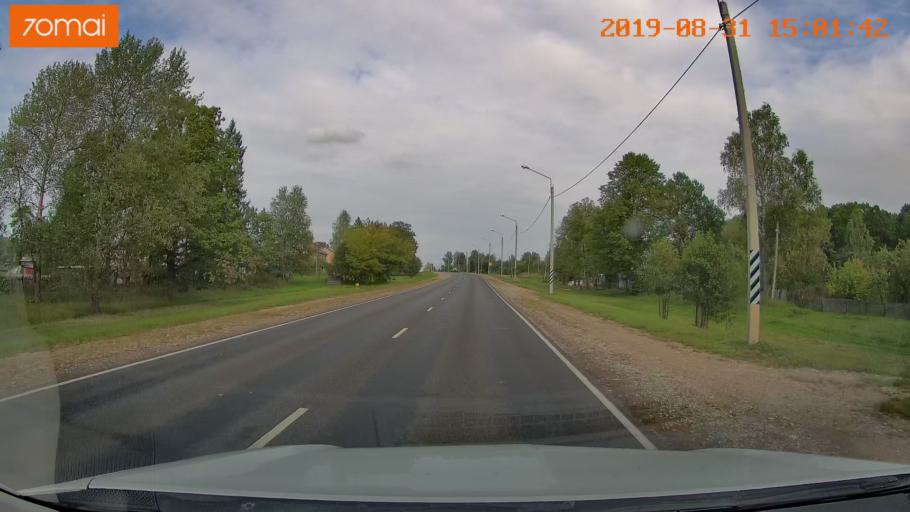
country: RU
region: Kaluga
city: Spas-Demensk
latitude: 54.3410
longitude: 34.0623
